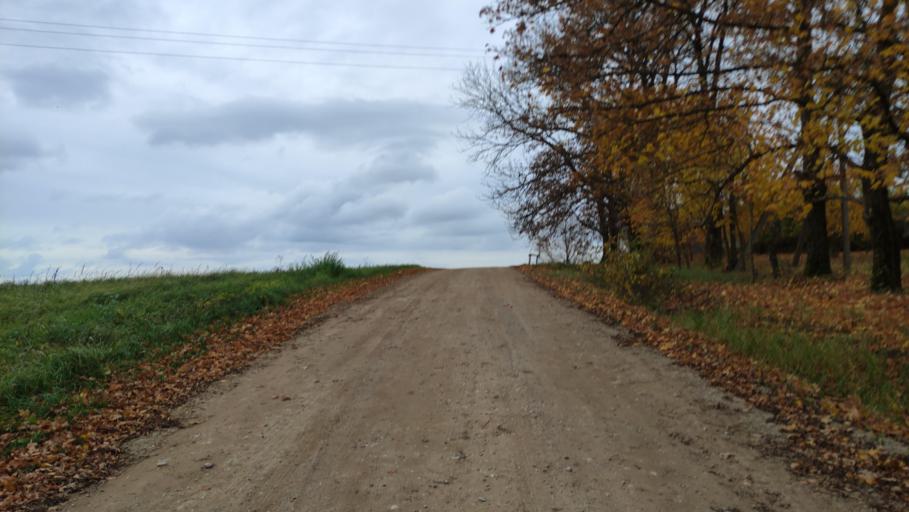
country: LT
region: Alytaus apskritis
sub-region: Alytus
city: Alytus
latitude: 54.4311
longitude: 23.8575
